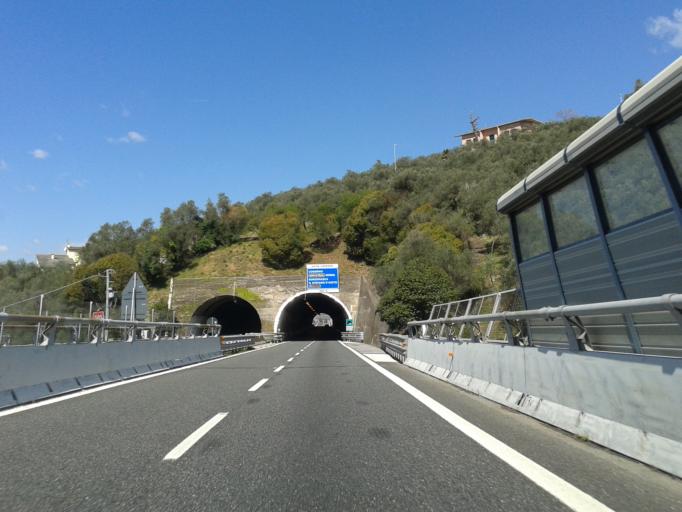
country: IT
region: Liguria
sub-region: Provincia di Genova
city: Lavagna
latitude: 44.3125
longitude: 9.3586
